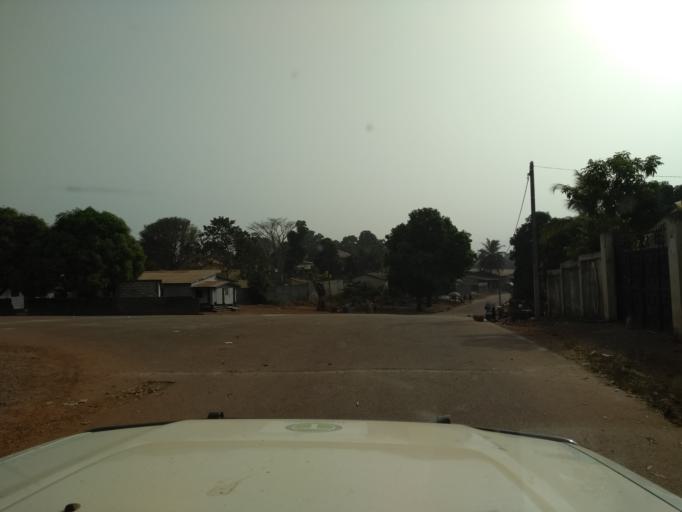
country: GN
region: Kindia
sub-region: Prefecture de Dubreka
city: Dubreka
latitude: 9.7874
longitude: -13.5219
